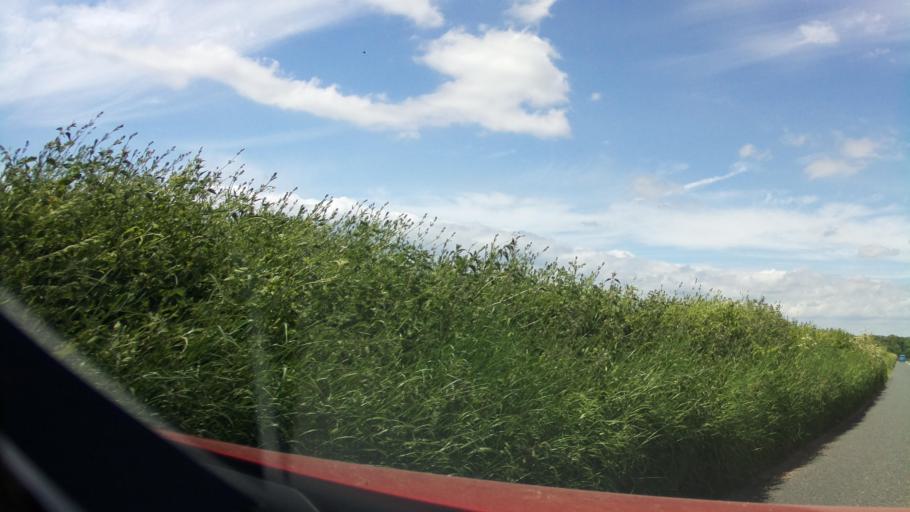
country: GB
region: Wales
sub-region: Monmouthshire
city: Monmouth
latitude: 51.7923
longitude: -2.7162
